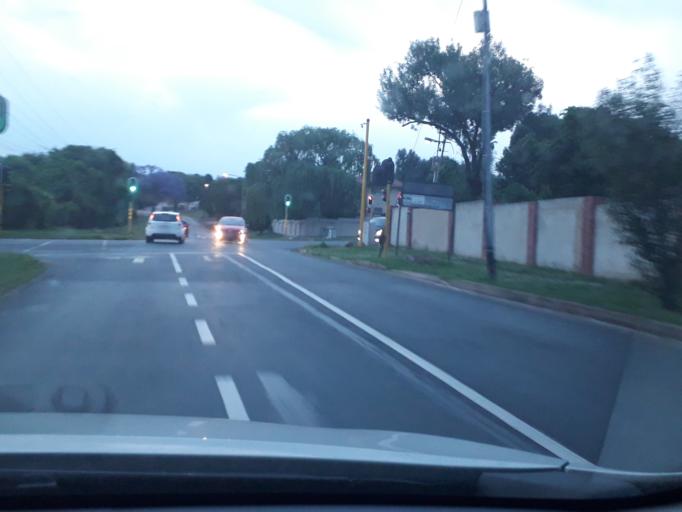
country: ZA
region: Gauteng
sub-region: City of Johannesburg Metropolitan Municipality
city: Johannesburg
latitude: -26.1493
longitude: 27.9946
